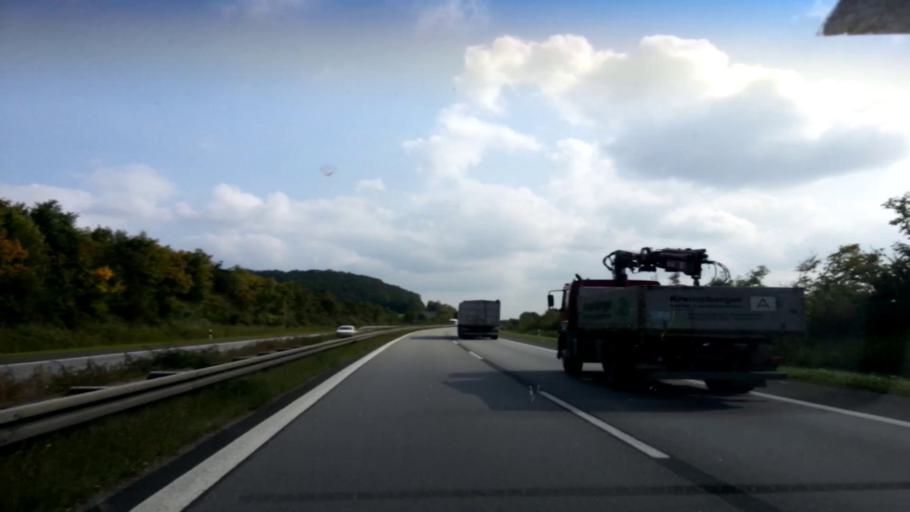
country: DE
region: Bavaria
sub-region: Regierungsbezirk Unterfranken
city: Stettfeld
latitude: 49.9575
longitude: 10.7432
